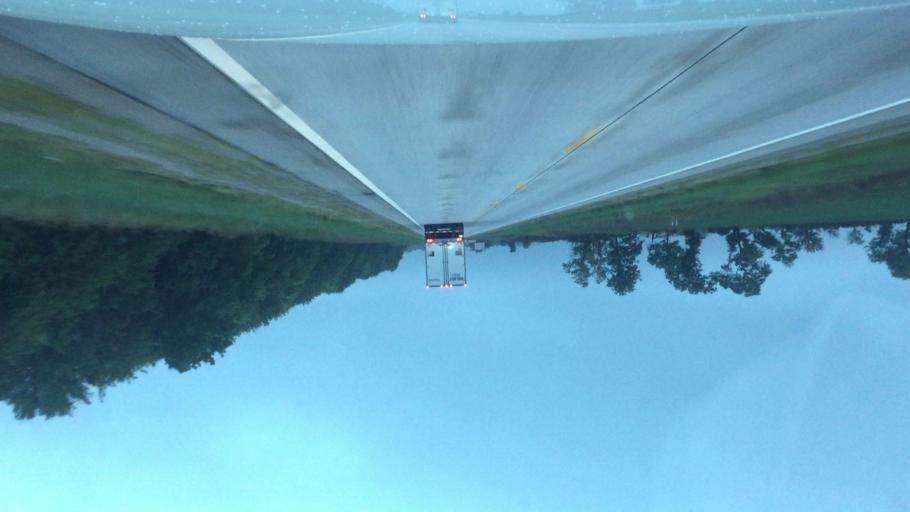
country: US
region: Kansas
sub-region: Neosho County
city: Chanute
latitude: 37.6361
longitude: -95.4796
